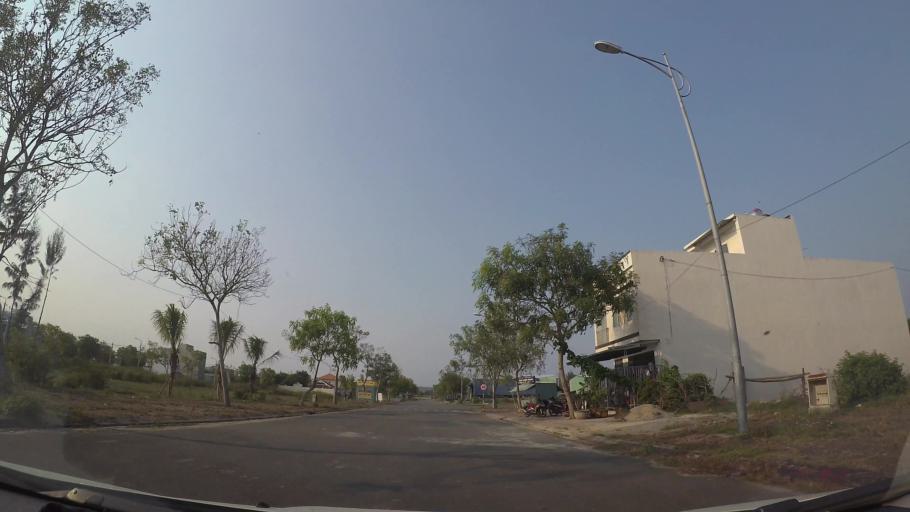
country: VN
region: Da Nang
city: Ngu Hanh Son
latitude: 15.9687
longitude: 108.2567
